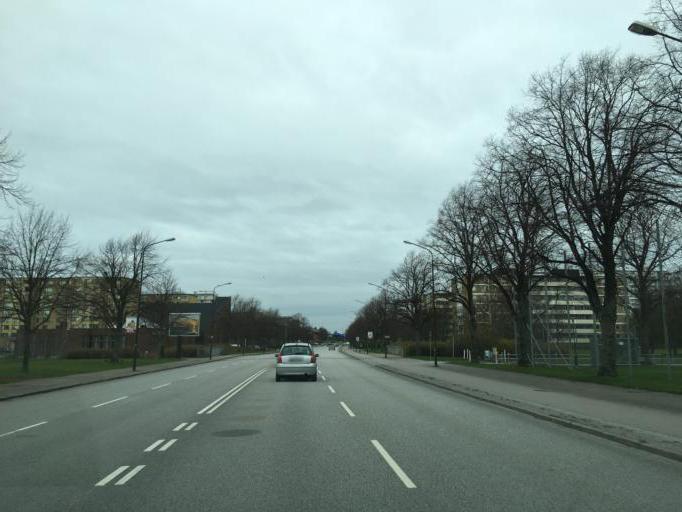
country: SE
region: Skane
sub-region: Malmo
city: Malmoe
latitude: 55.5817
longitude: 12.9856
